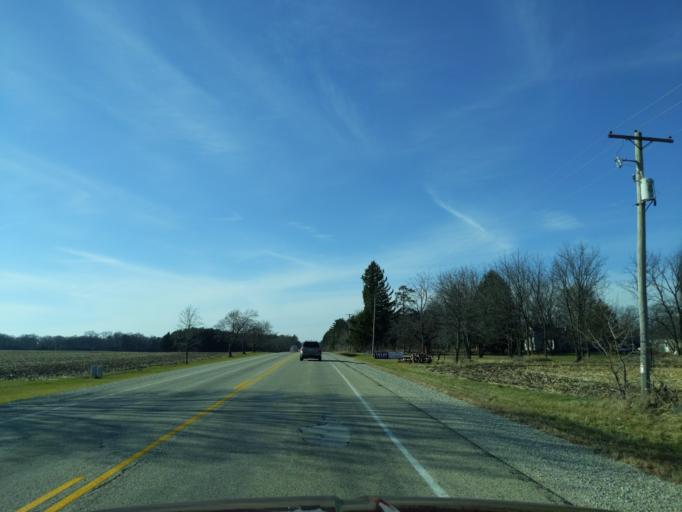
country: US
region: Wisconsin
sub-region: Walworth County
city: Whitewater
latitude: 42.8274
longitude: -88.7816
